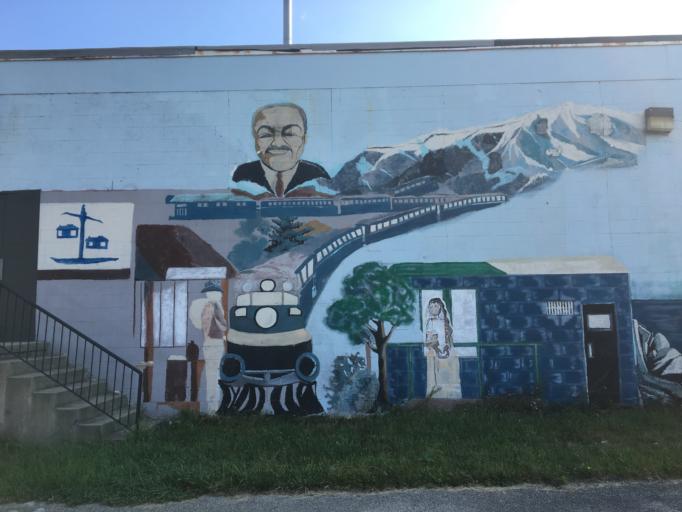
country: US
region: Michigan
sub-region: Wayne County
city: Hamtramck
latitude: 42.3746
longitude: -83.0087
